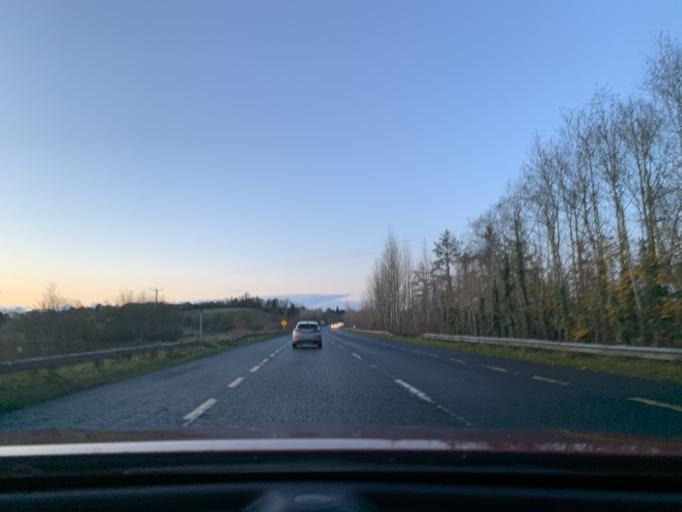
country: IE
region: Connaught
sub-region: County Leitrim
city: Carrick-on-Shannon
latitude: 53.9232
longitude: -7.9932
